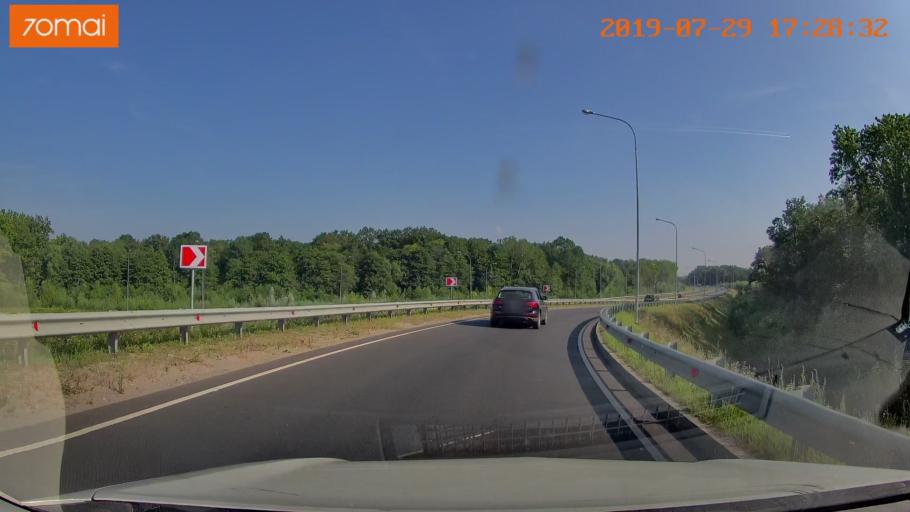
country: RU
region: Kaliningrad
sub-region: Gorod Kaliningrad
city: Kaliningrad
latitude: 54.7624
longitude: 20.4697
